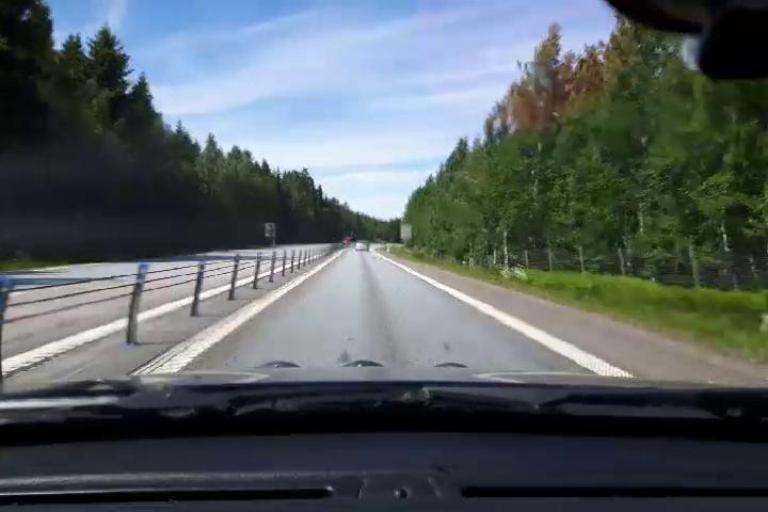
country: SE
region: Gaevleborg
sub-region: Gavle Kommun
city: Norrsundet
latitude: 60.9231
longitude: 17.0113
